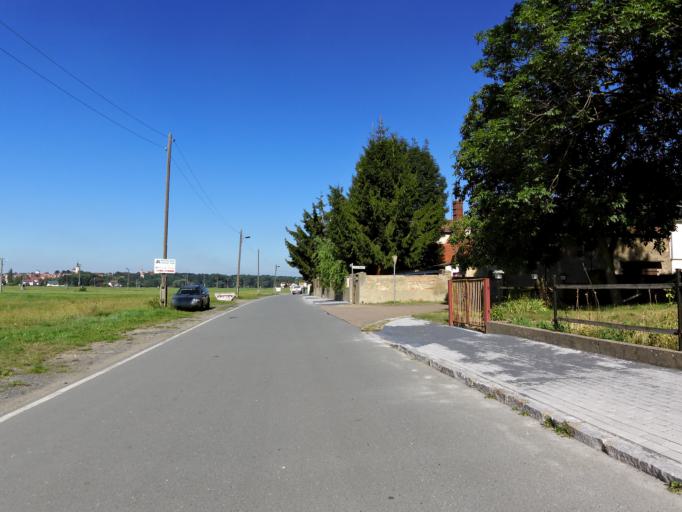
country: DE
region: Saxony
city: Strehla
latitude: 51.3524
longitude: 13.2492
